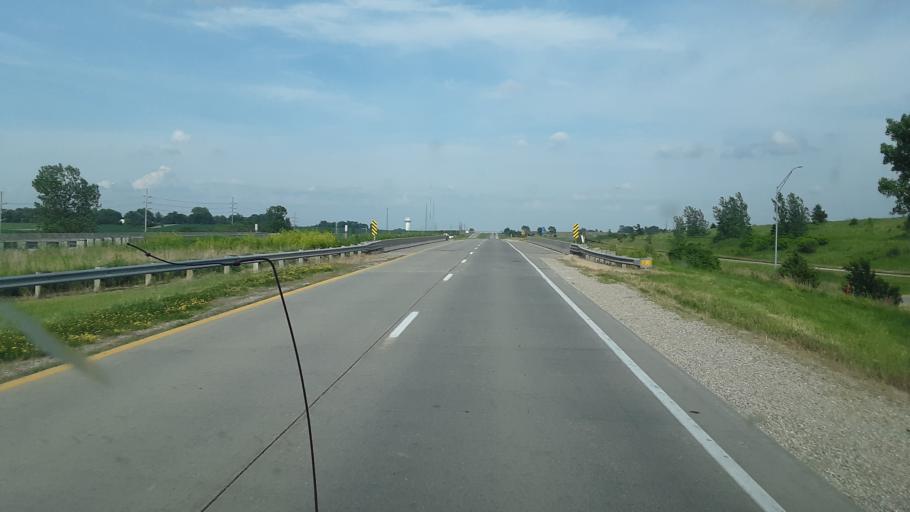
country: US
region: Iowa
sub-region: Marshall County
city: Marshalltown
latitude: 42.0033
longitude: -92.9618
